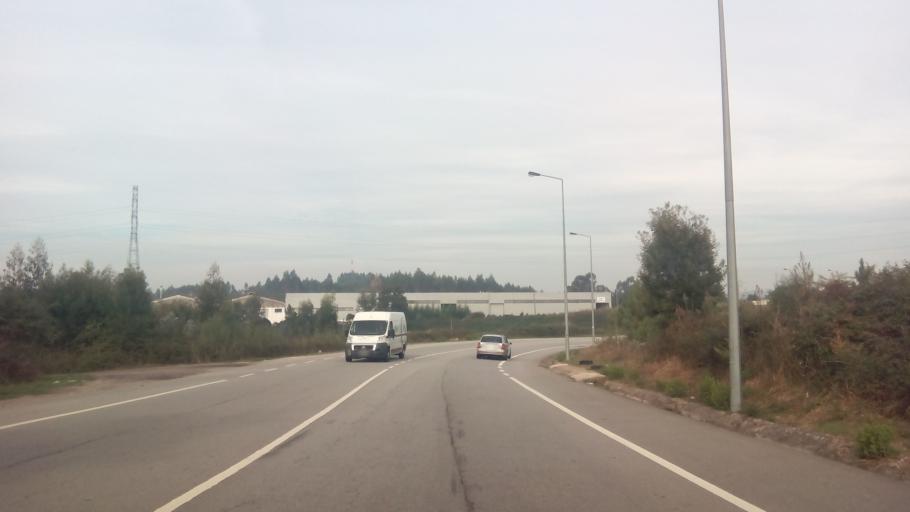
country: PT
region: Porto
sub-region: Paredes
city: Gandra
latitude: 41.1987
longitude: -8.4376
